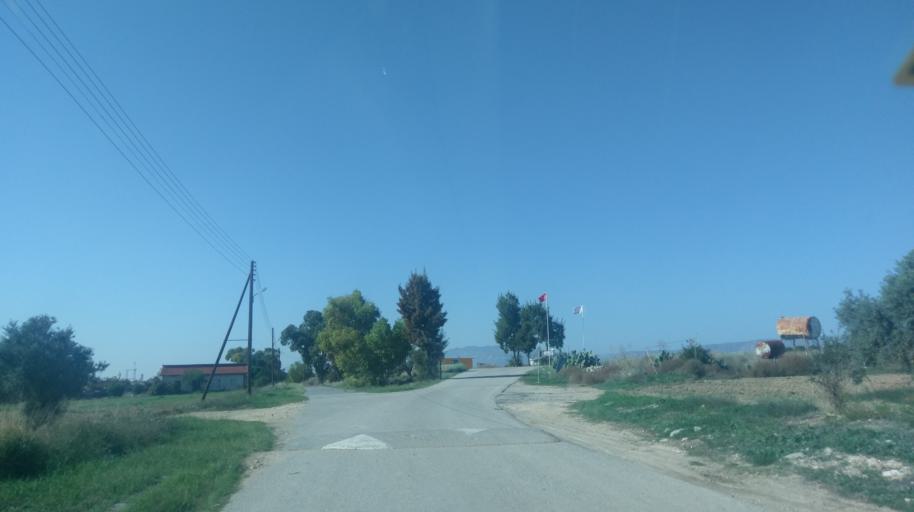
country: CY
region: Ammochostos
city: Lefkonoiko
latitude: 35.2610
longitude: 33.7802
